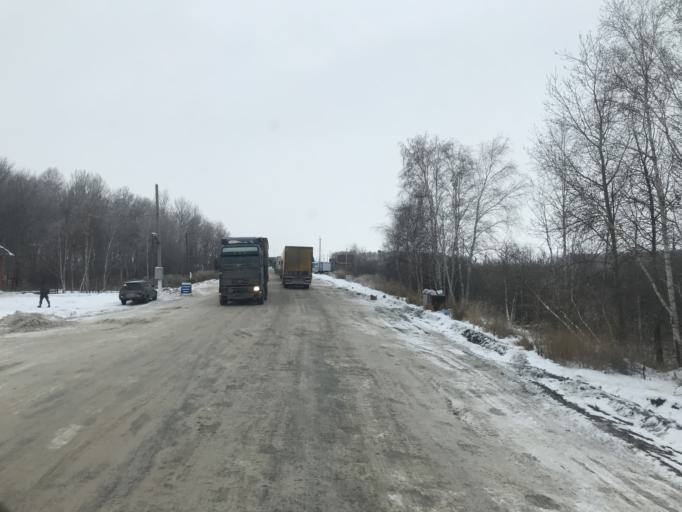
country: RU
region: Kurgan
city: Petukhovo
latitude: 55.0941
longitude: 68.2823
